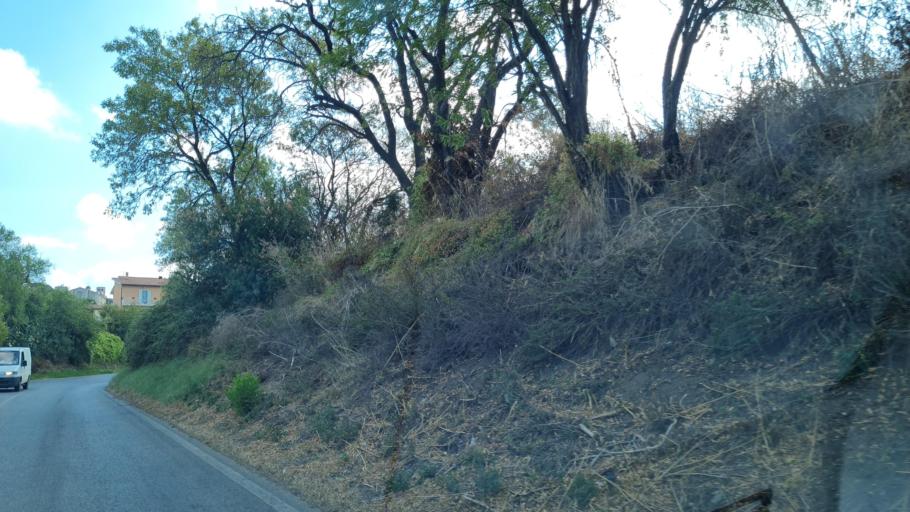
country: IT
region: Latium
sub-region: Provincia di Viterbo
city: Tarquinia
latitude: 42.2521
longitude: 11.7472
